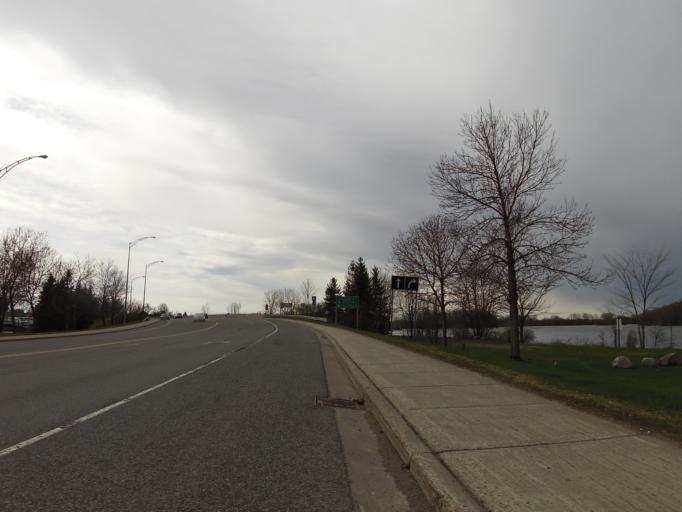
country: CA
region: Ontario
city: Hawkesbury
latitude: 45.6140
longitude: -74.6026
